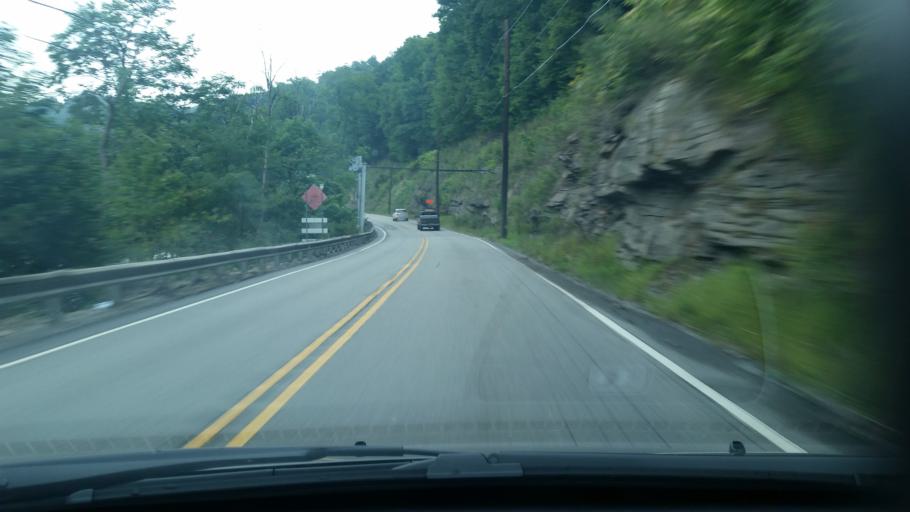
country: US
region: Pennsylvania
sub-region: Clearfield County
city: Shiloh
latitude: 41.0697
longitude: -78.3644
